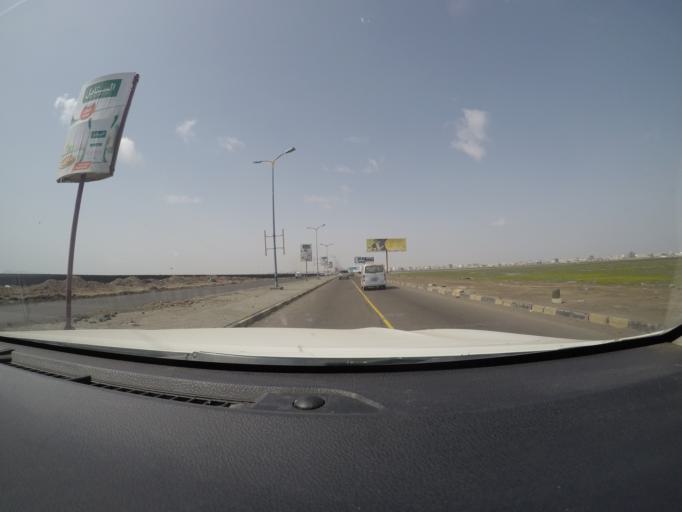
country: YE
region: Aden
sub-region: Khur Maksar
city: Khawr Maksar
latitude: 12.8426
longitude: 45.0248
